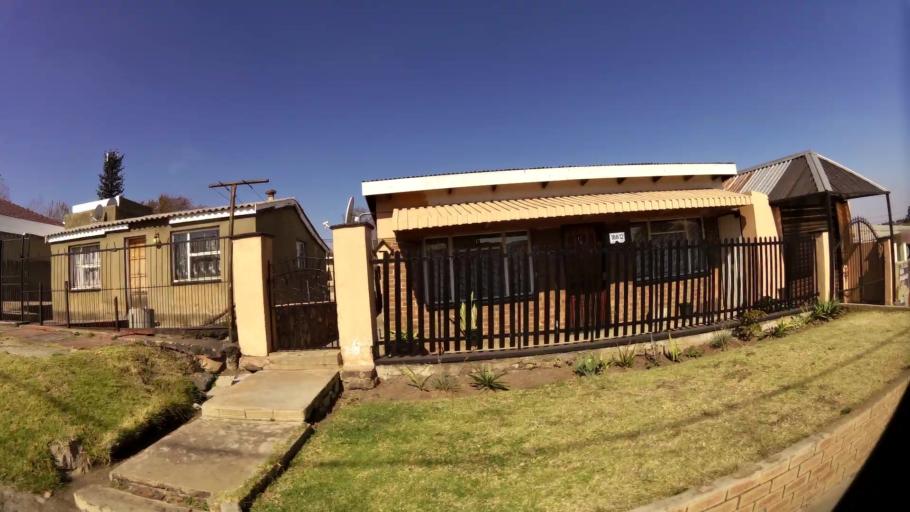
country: ZA
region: Gauteng
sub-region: City of Johannesburg Metropolitan Municipality
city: Soweto
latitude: -26.2309
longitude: 27.8888
